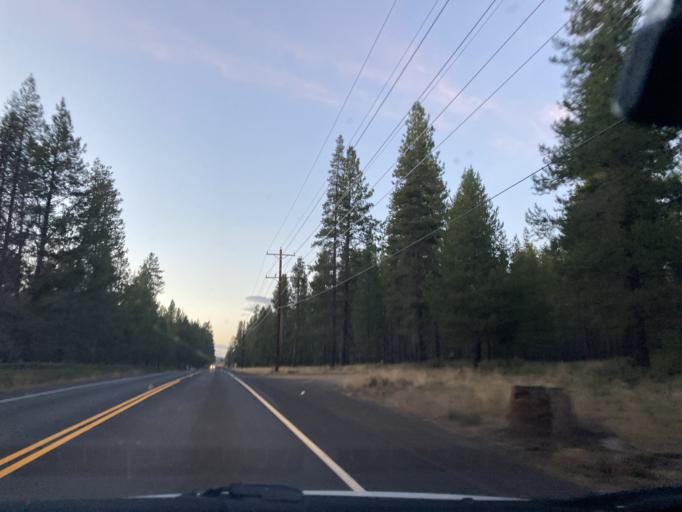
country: US
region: Oregon
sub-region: Deschutes County
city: Three Rivers
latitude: 43.8376
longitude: -121.4419
